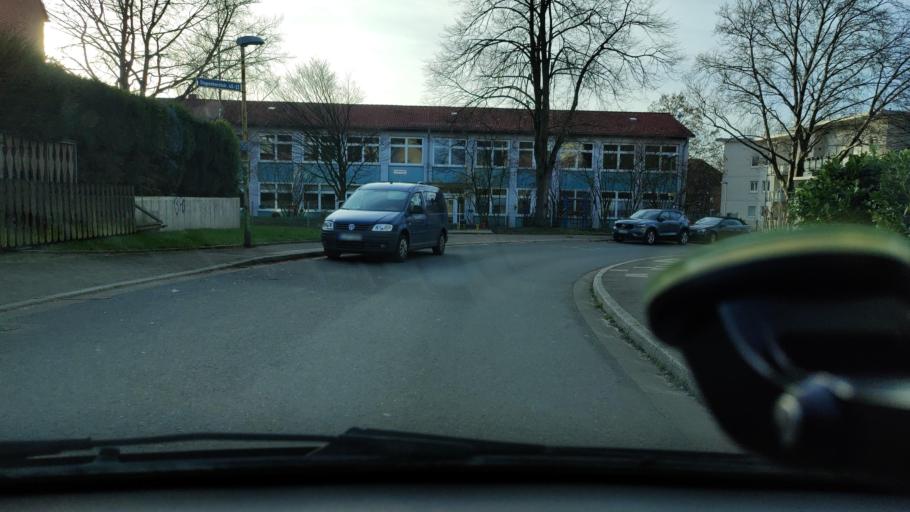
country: DE
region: North Rhine-Westphalia
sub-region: Regierungsbezirk Dusseldorf
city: Essen
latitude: 51.5089
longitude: 7.0063
